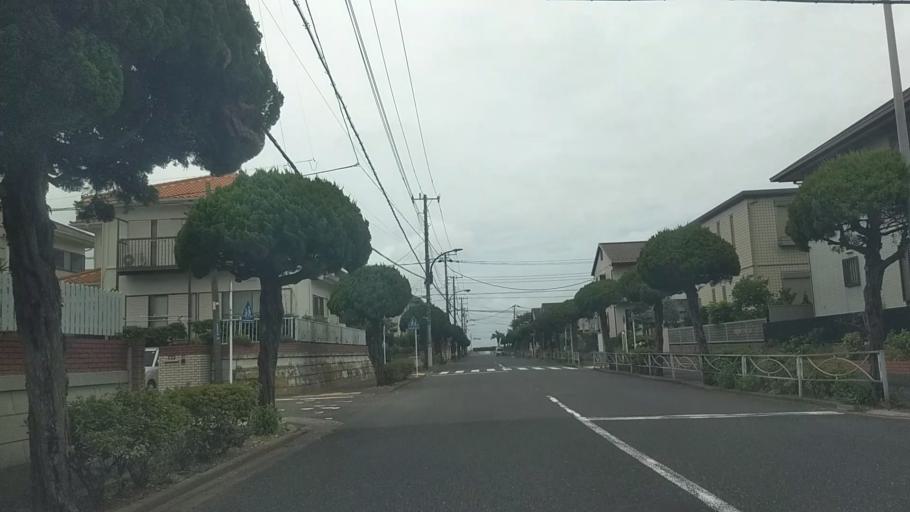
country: JP
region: Kanagawa
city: Yokosuka
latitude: 35.2613
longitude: 139.7081
